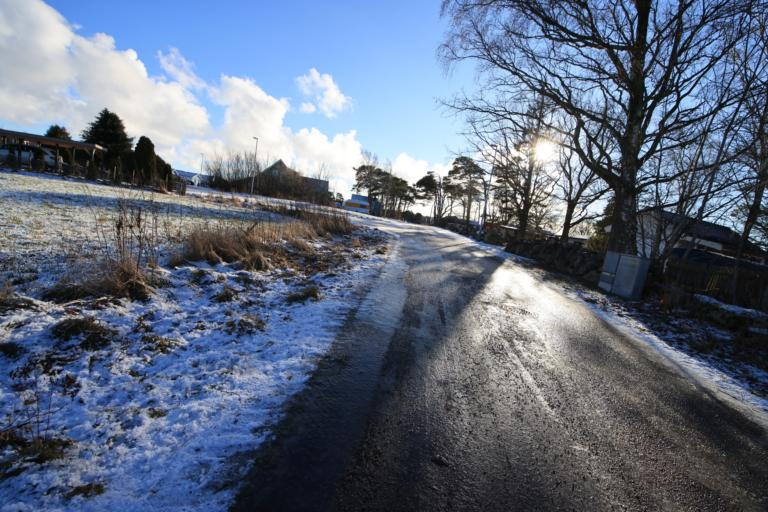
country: SE
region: Halland
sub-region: Varbergs Kommun
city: Traslovslage
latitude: 57.0670
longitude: 12.2863
